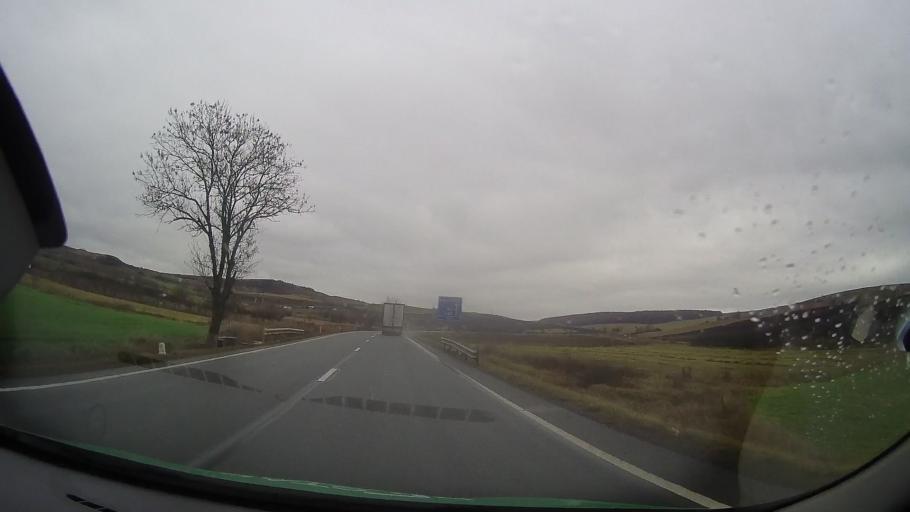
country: RO
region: Mures
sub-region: Comuna Lunca
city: Lunca
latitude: 46.8719
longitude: 24.5507
